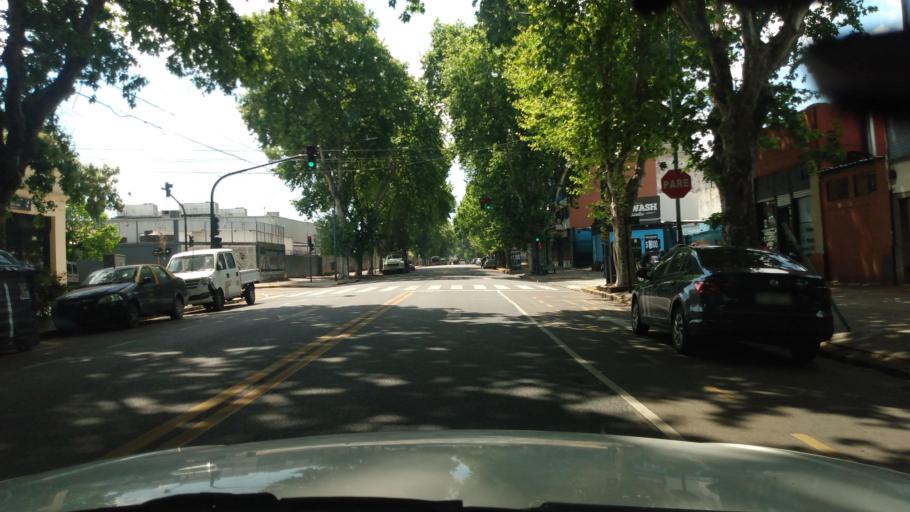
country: AR
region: Buenos Aires
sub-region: Partido de General San Martin
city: General San Martin
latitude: -34.5759
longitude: -58.5068
